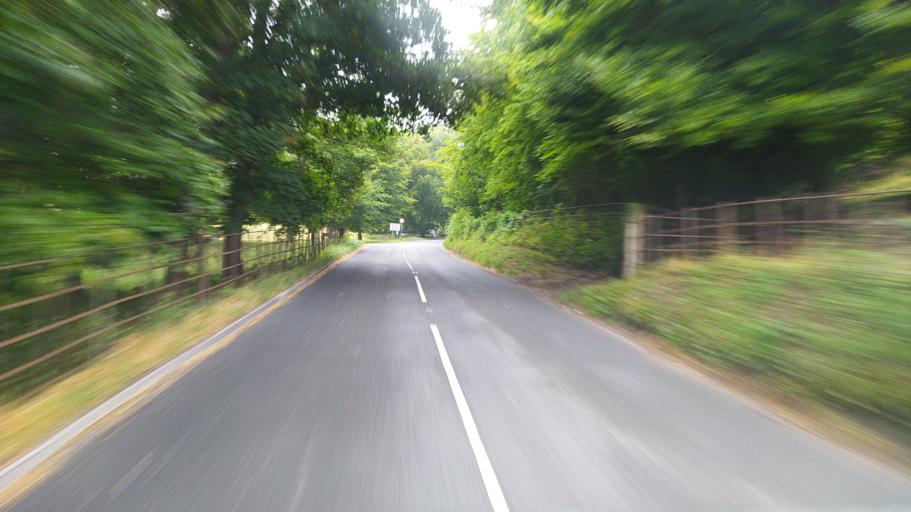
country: GB
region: England
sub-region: Wiltshire
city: Ansty
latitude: 50.9542
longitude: -2.0744
